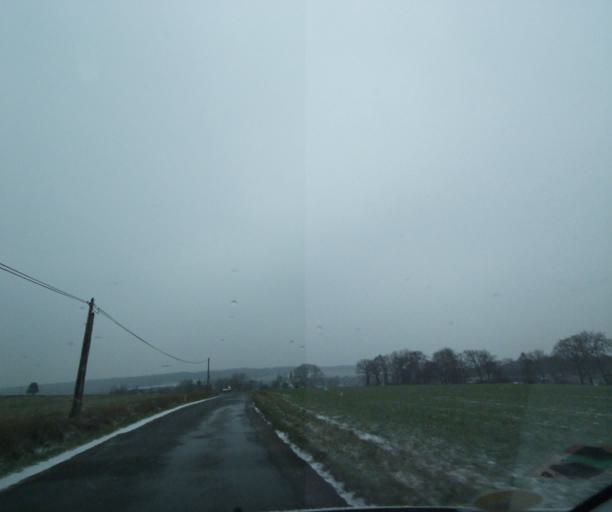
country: FR
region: Champagne-Ardenne
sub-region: Departement de la Haute-Marne
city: Wassy
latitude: 48.4702
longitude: 4.9791
